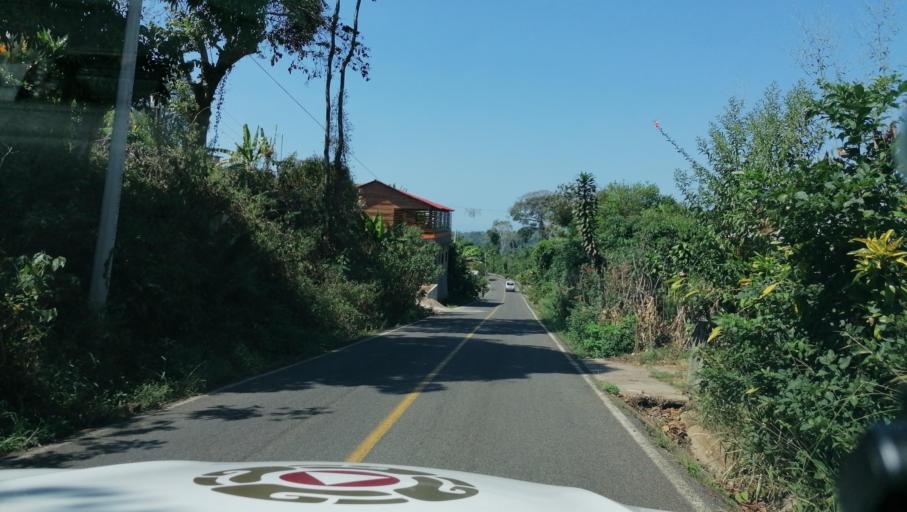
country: MX
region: Chiapas
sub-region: Cacahoatan
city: Benito Juarez
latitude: 15.0184
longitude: -92.2238
